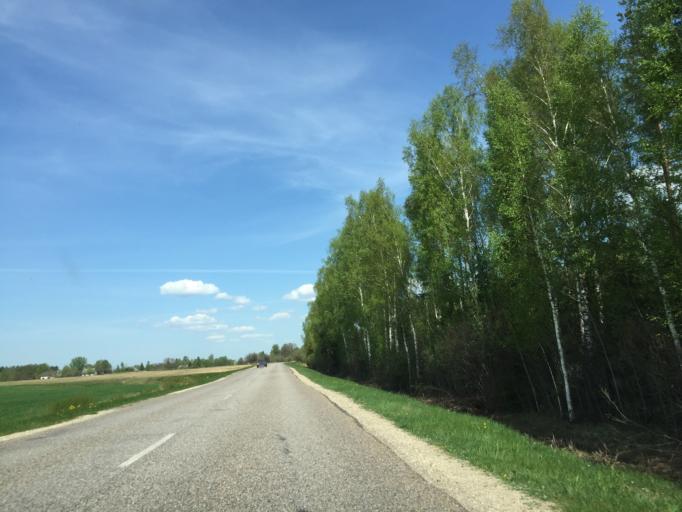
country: LV
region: Krimulda
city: Ragana
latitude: 57.3155
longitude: 24.6426
